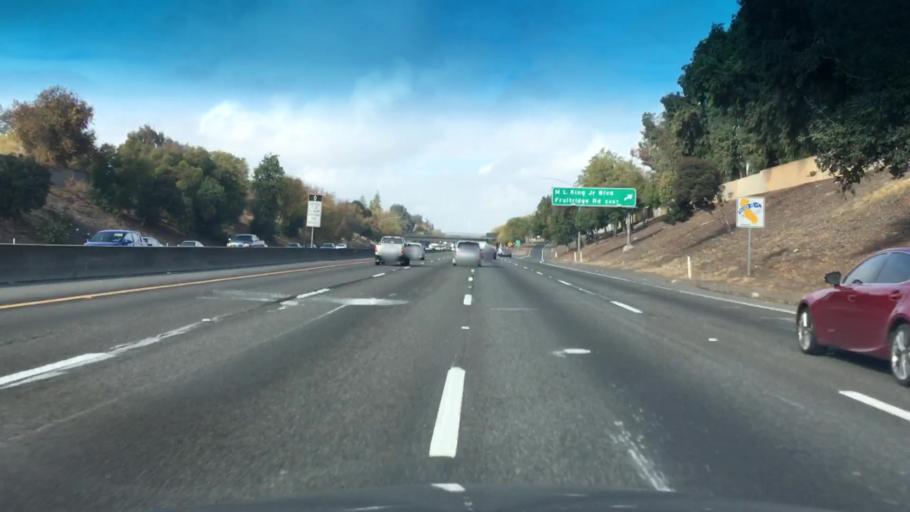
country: US
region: California
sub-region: Sacramento County
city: Parkway
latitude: 38.5165
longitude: -121.4630
